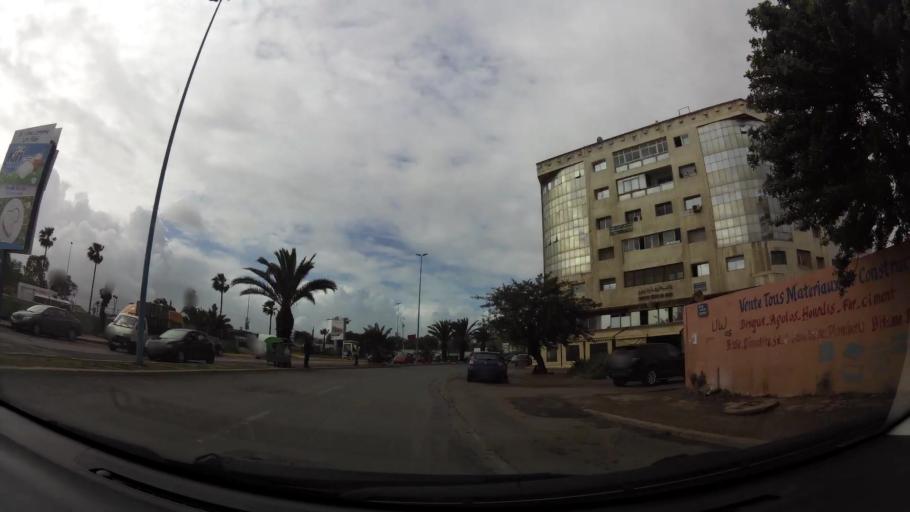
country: MA
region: Grand Casablanca
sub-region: Casablanca
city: Casablanca
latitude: 33.5628
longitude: -7.6683
